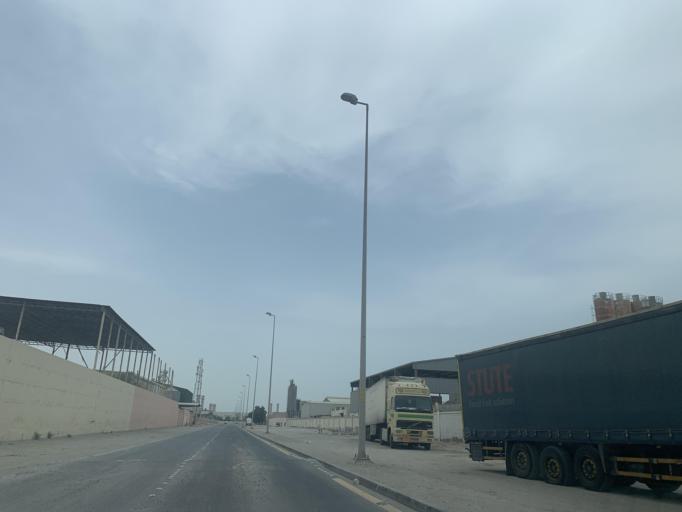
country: BH
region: Muharraq
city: Al Hadd
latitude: 26.2060
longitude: 50.6627
